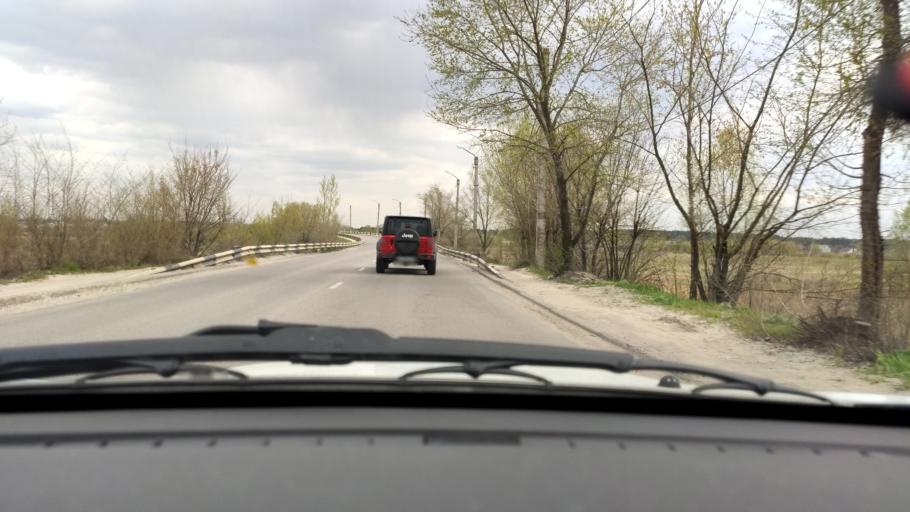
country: RU
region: Voronezj
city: Somovo
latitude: 51.7437
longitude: 39.3409
